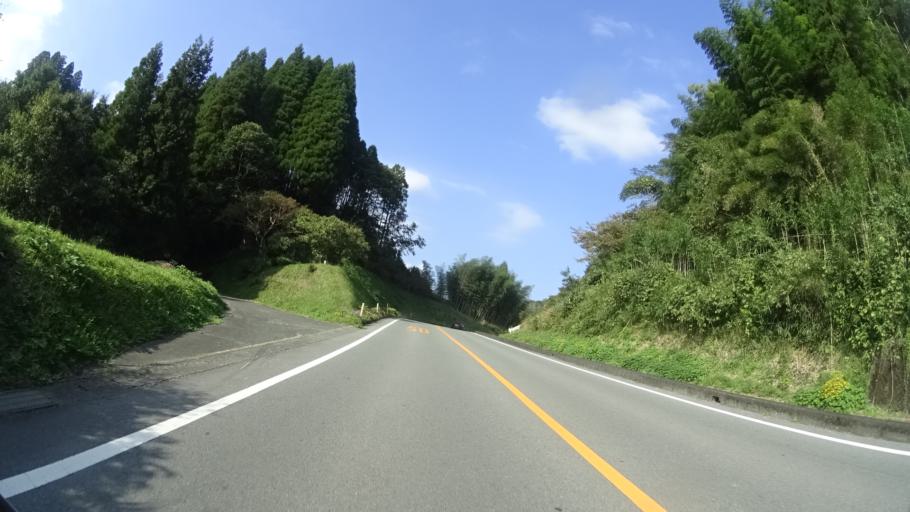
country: JP
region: Oita
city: Tsukawaki
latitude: 33.1284
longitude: 131.0859
